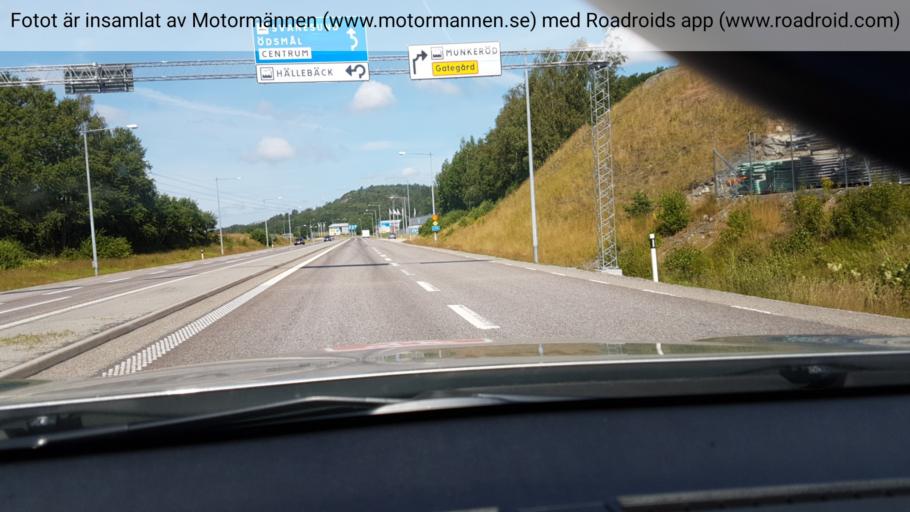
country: SE
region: Vaestra Goetaland
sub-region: Stenungsunds Kommun
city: Stenungsund
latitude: 58.0607
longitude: 11.8725
